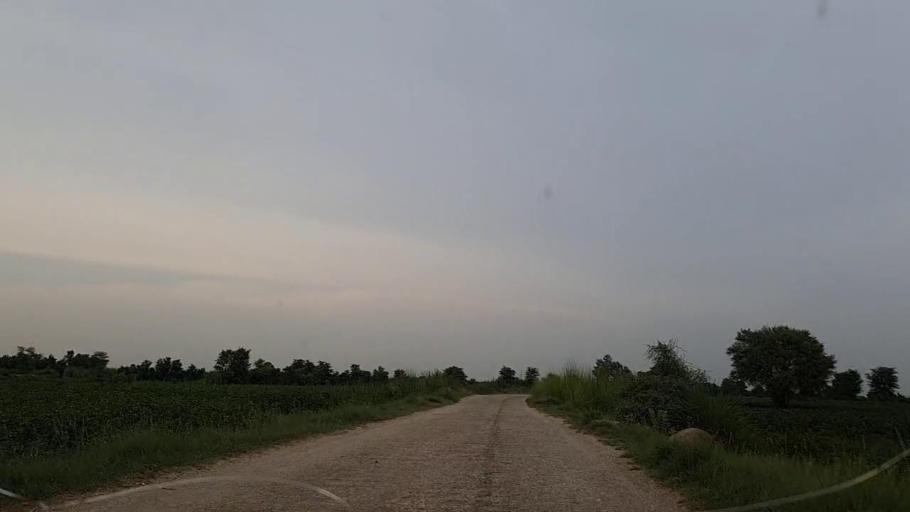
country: PK
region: Sindh
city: Mirpur Mathelo
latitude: 27.8738
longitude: 69.6357
